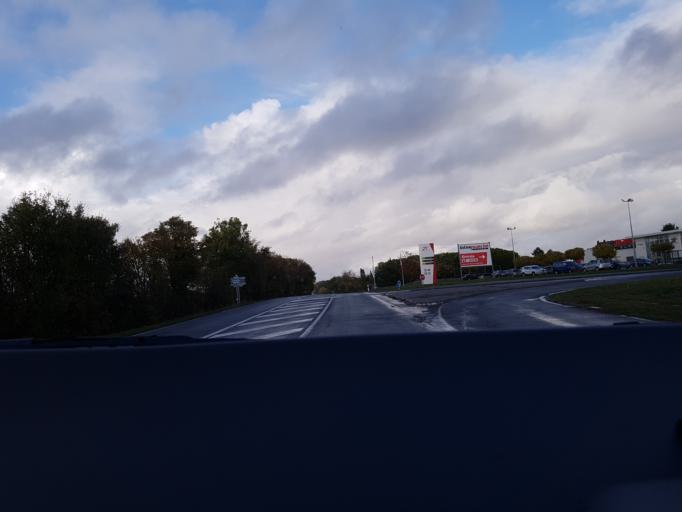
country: FR
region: Poitou-Charentes
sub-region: Departement de la Charente-Maritime
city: Aulnay
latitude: 46.0310
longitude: -0.3493
